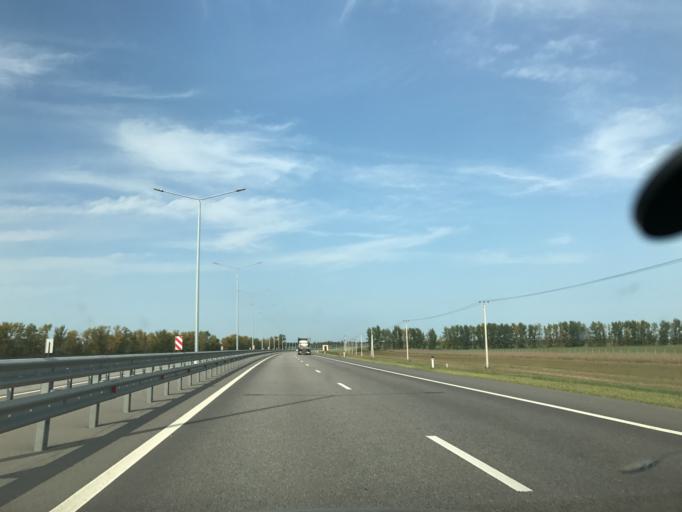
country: RU
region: Voronezj
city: Podkletnoye
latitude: 51.5108
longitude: 39.5137
